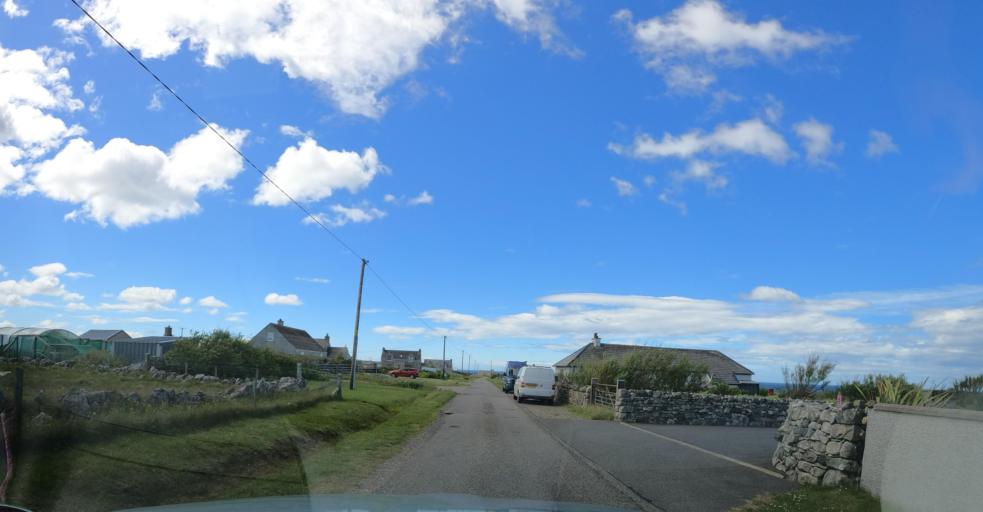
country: GB
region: Scotland
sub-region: Eilean Siar
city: Isle of Lewis
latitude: 58.3578
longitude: -6.5578
